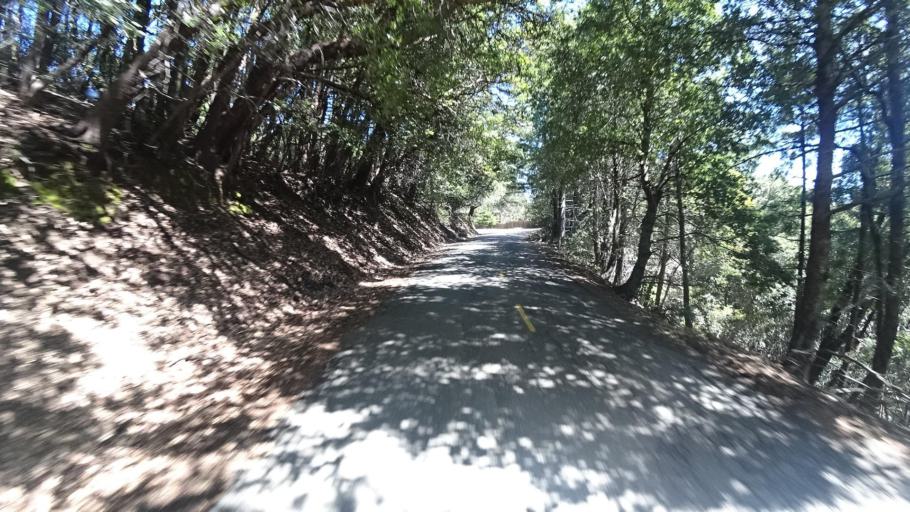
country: US
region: California
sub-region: Humboldt County
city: Rio Dell
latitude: 40.2760
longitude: -124.0715
